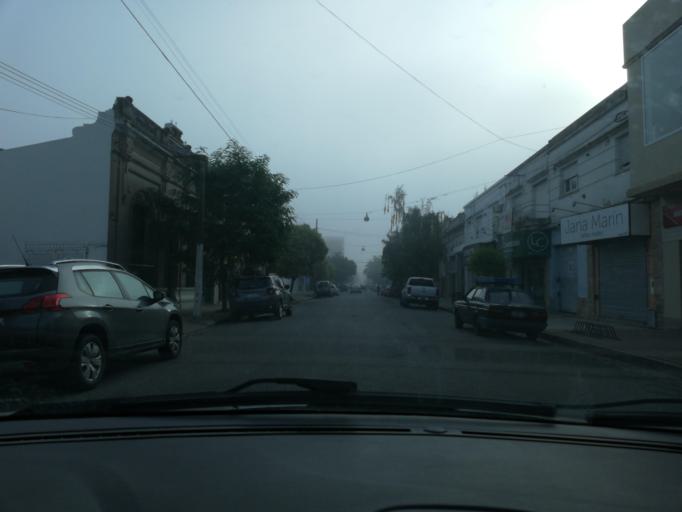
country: AR
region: Buenos Aires
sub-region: Partido de Balcarce
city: Balcarce
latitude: -37.8502
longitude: -58.2581
